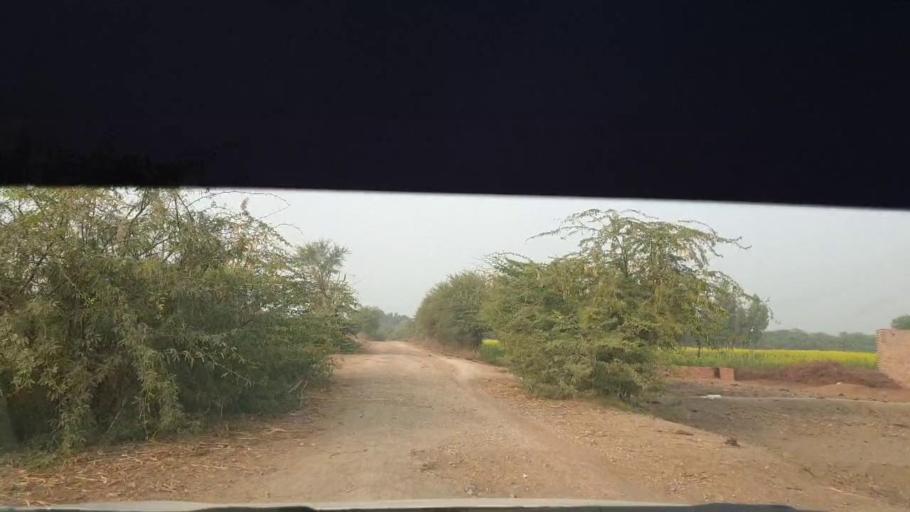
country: PK
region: Sindh
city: Berani
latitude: 25.8293
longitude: 68.8914
